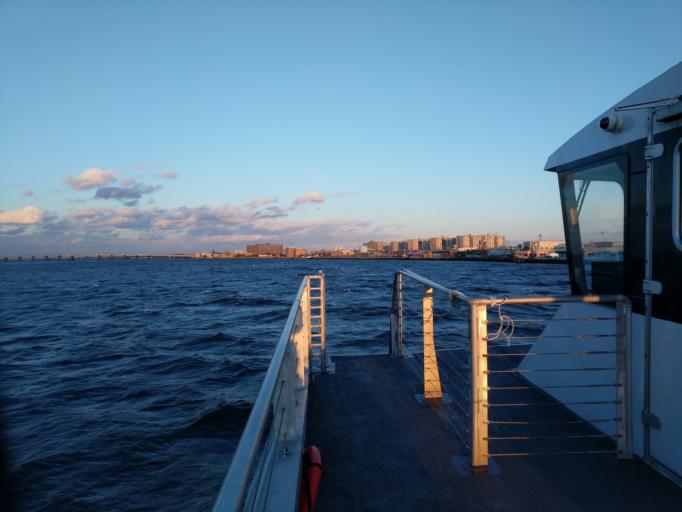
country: US
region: New York
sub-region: Kings County
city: East New York
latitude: 40.5837
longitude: -73.8405
